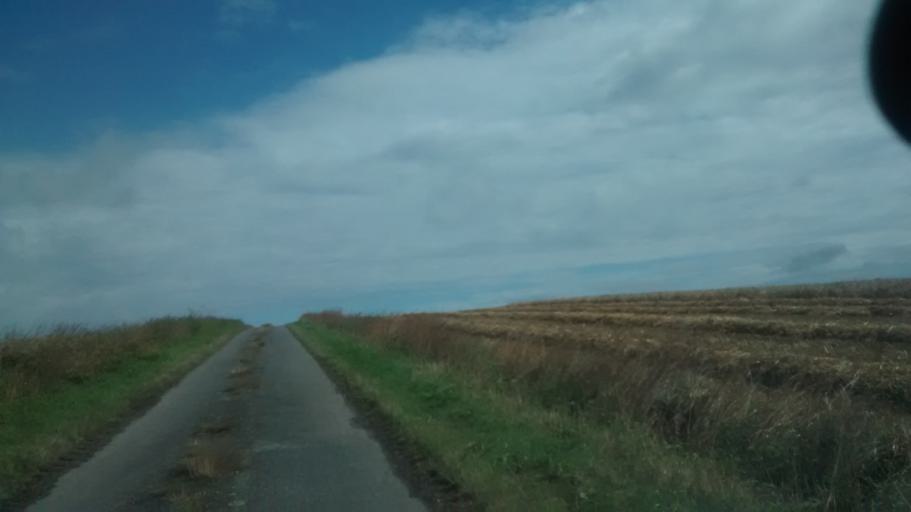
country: FR
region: Brittany
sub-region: Departement d'Ille-et-Vilaine
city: La Dominelais
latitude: 47.7850
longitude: -1.7162
